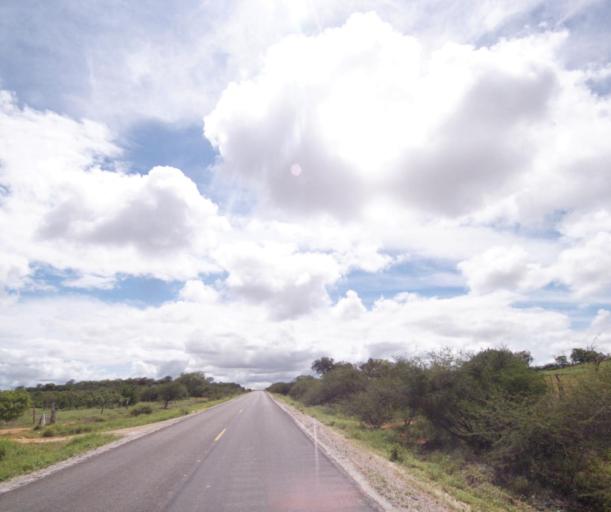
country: BR
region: Bahia
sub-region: Tanhacu
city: Tanhacu
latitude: -14.1579
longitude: -41.2444
